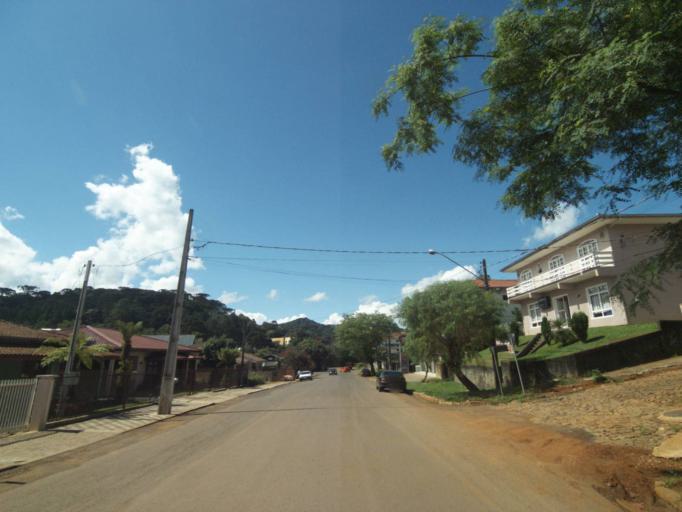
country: BR
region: Parana
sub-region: Uniao Da Vitoria
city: Uniao da Vitoria
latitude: -26.1580
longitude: -51.5530
